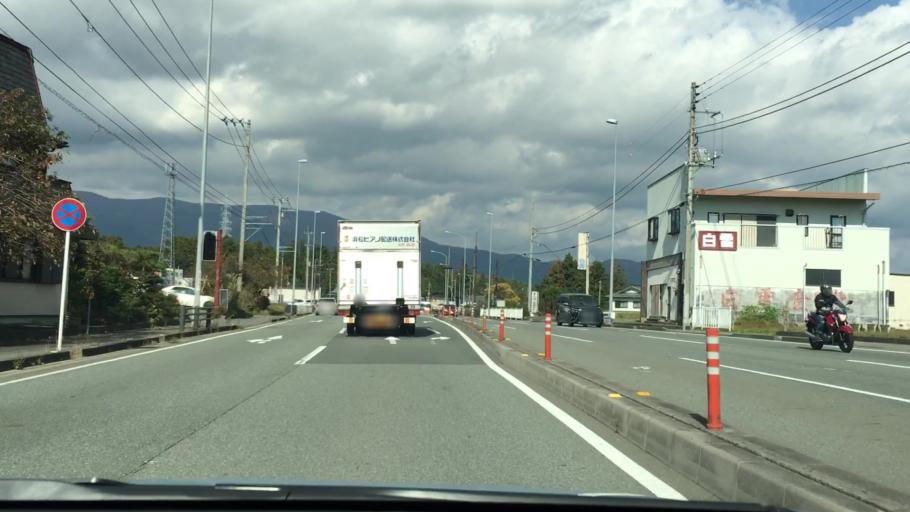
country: JP
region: Shizuoka
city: Gotemba
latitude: 35.3262
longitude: 138.9319
